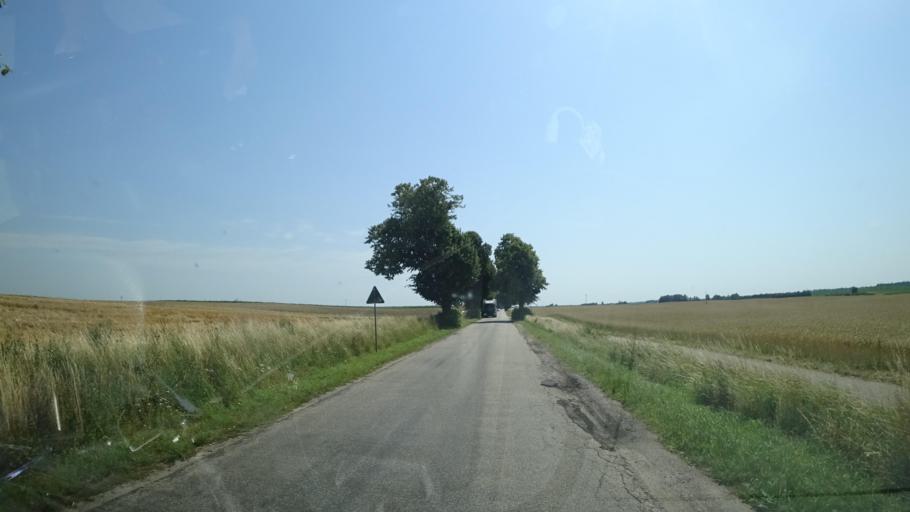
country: PL
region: Pomeranian Voivodeship
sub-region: Powiat chojnicki
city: Brusy
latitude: 53.8817
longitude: 17.6437
